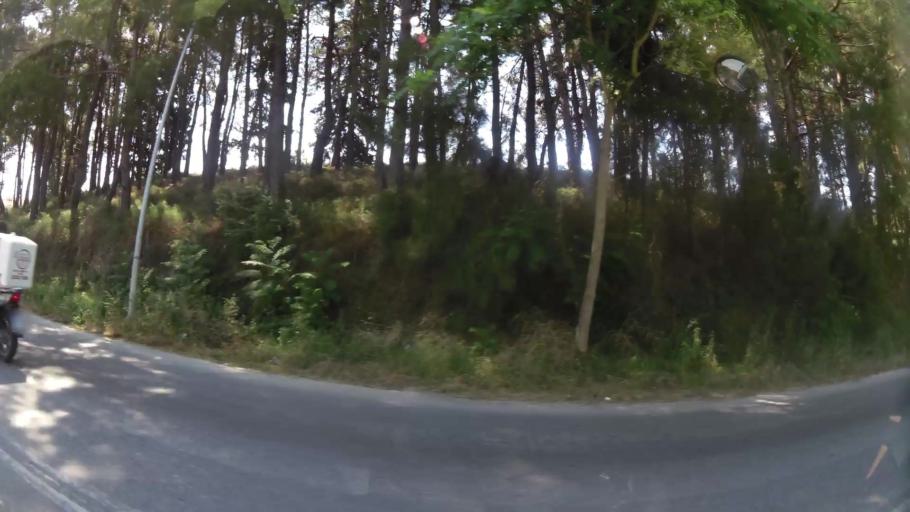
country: GR
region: Central Macedonia
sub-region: Nomos Thessalonikis
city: Neoi Epivates
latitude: 40.5000
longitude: 22.9066
